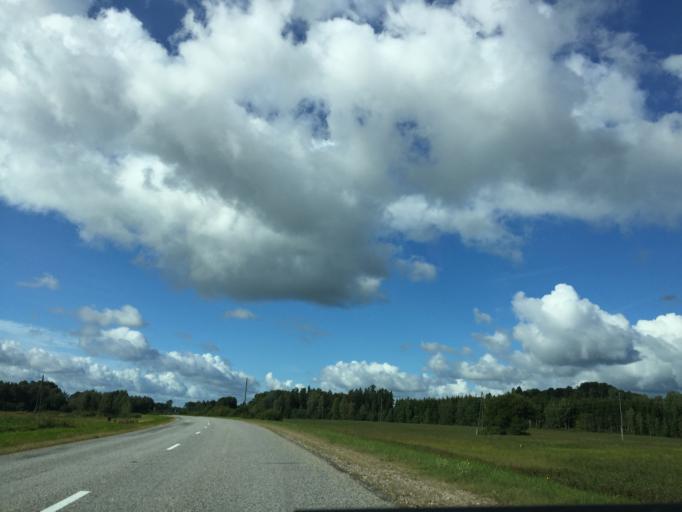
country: LV
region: Kuldigas Rajons
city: Kuldiga
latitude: 56.9934
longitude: 22.0926
